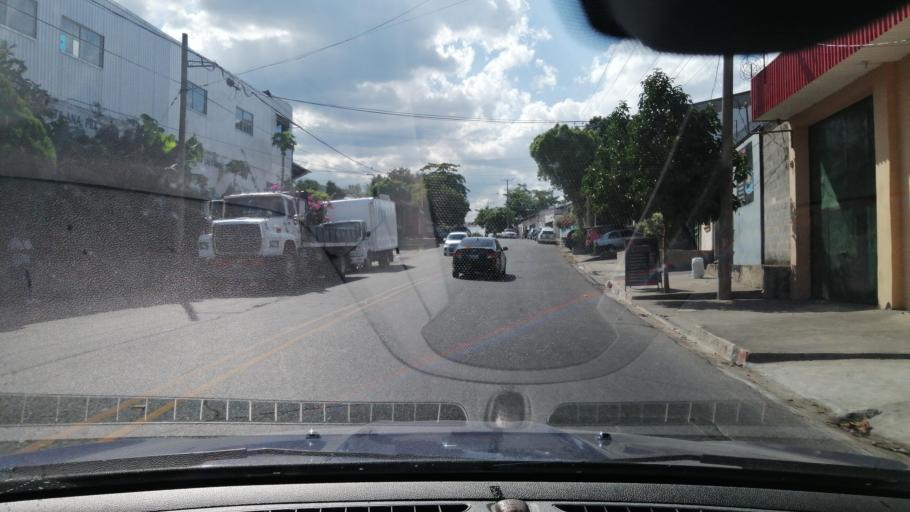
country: SV
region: Santa Ana
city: Santa Ana
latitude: 13.9819
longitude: -89.5556
